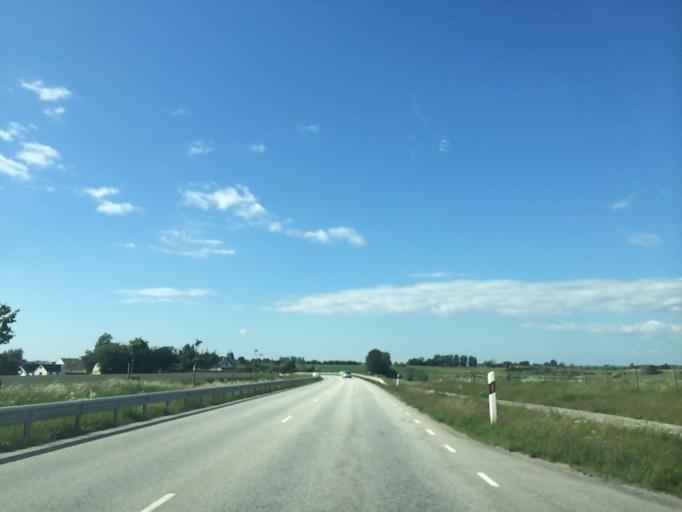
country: SE
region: Skane
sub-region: Kavlinge Kommun
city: Loddekopinge
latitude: 55.7496
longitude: 13.0277
